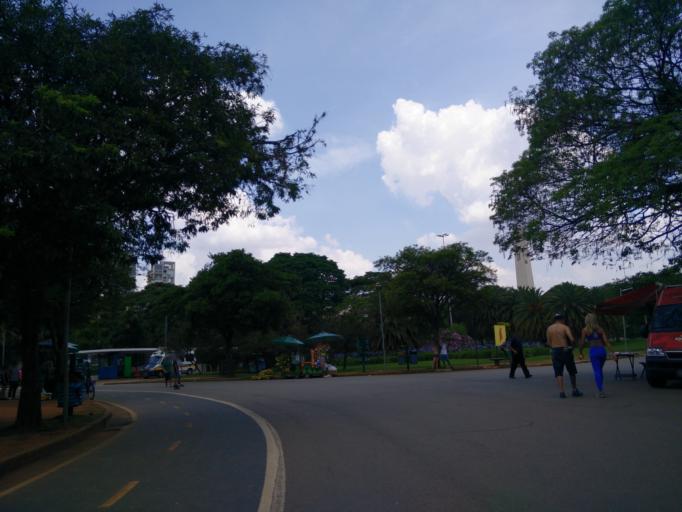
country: BR
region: Sao Paulo
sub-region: Sao Paulo
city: Sao Paulo
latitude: -23.5835
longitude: -46.6582
